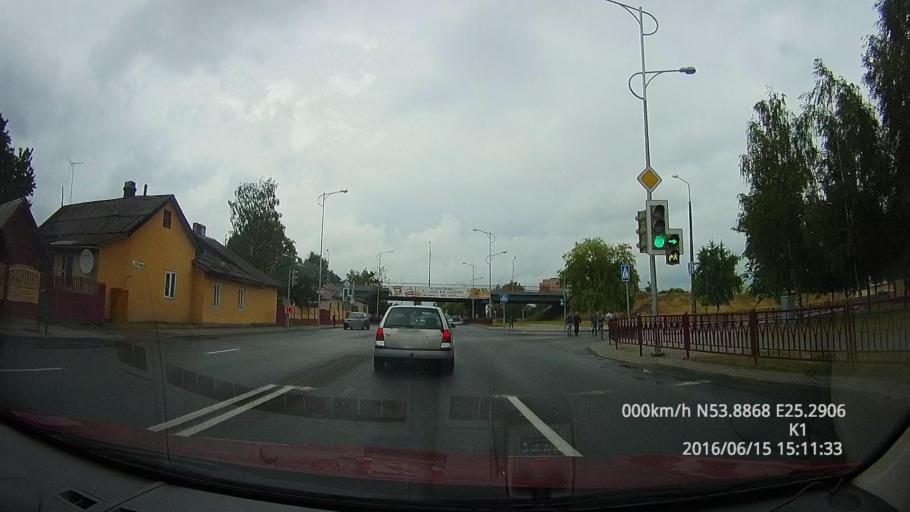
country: BY
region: Grodnenskaya
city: Lida
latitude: 53.8868
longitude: 25.2906
